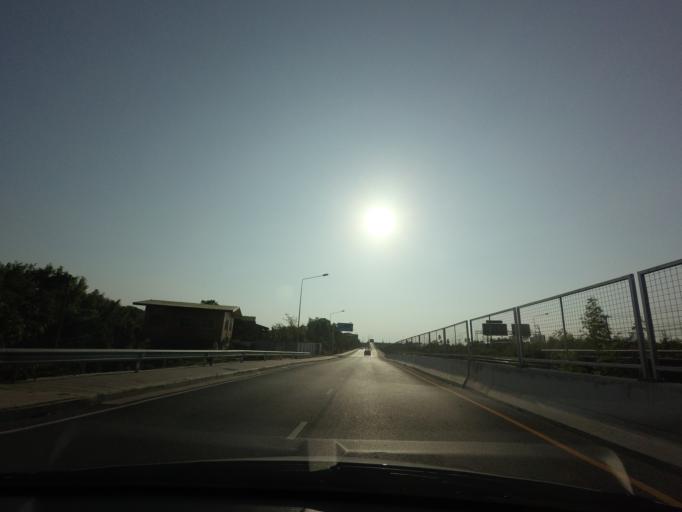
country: TH
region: Bangkok
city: Taling Chan
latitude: 13.7994
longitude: 100.4164
